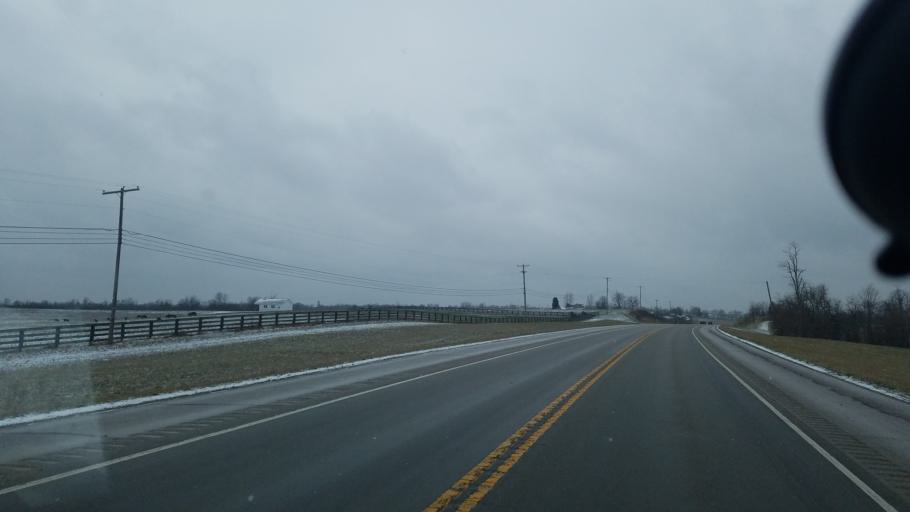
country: US
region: Kentucky
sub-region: Bath County
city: Owingsville
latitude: 38.2410
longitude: -83.8816
